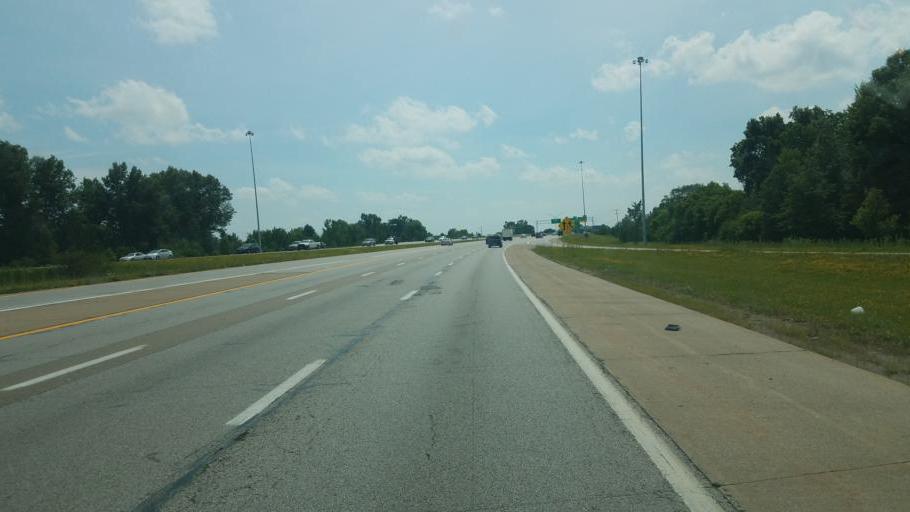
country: US
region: Ohio
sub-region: Franklin County
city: Gahanna
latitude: 40.0105
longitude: -82.9089
